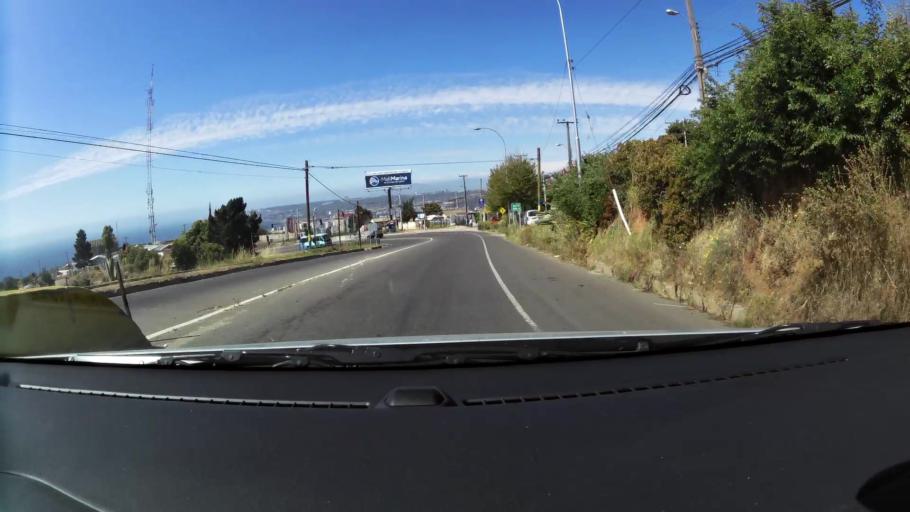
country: CL
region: Valparaiso
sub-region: Provincia de Valparaiso
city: Vina del Mar
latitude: -33.0413
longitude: -71.5695
